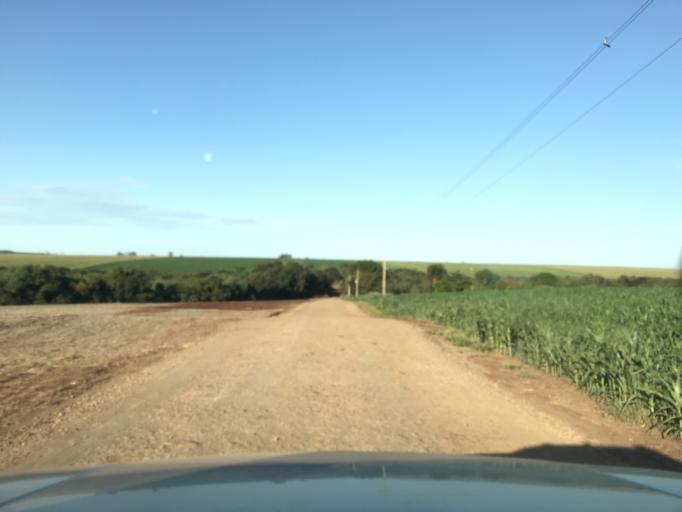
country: BR
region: Parana
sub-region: Palotina
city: Palotina
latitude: -24.2532
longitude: -53.7324
